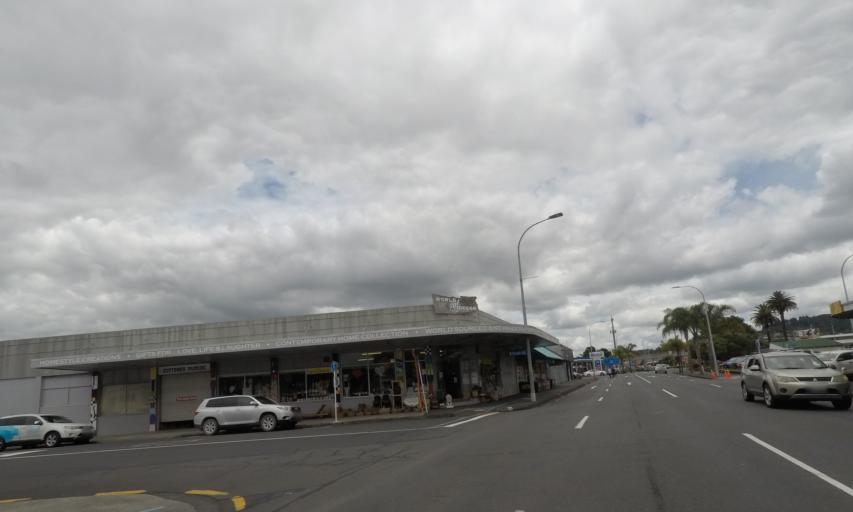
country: NZ
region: Northland
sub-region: Whangarei
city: Whangarei
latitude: -35.7268
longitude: 174.3215
